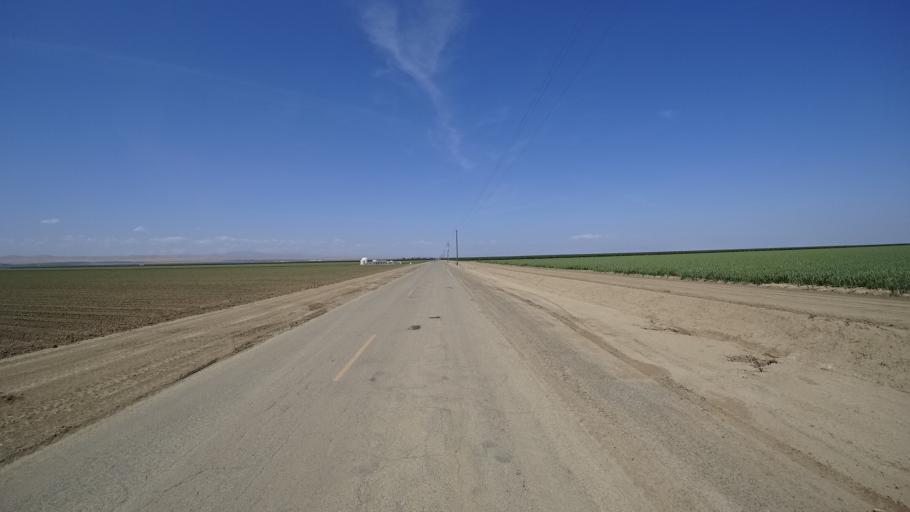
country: US
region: California
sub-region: Kings County
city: Kettleman City
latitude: 36.0943
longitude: -119.9744
